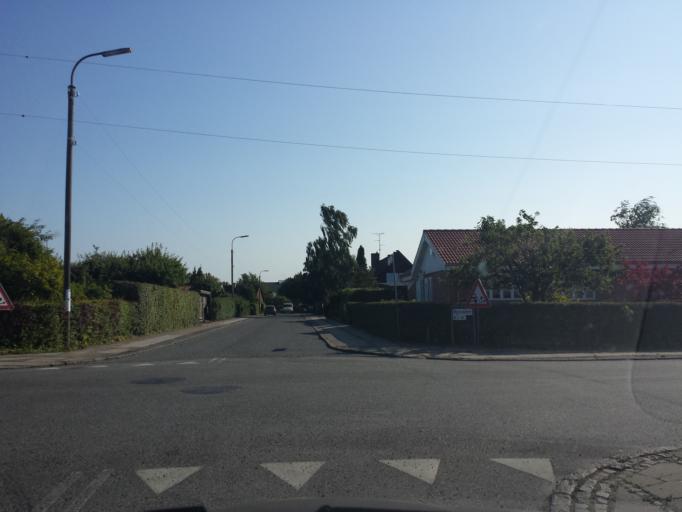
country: DK
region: Capital Region
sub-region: Herlev Kommune
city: Herlev
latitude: 55.7242
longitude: 12.4130
